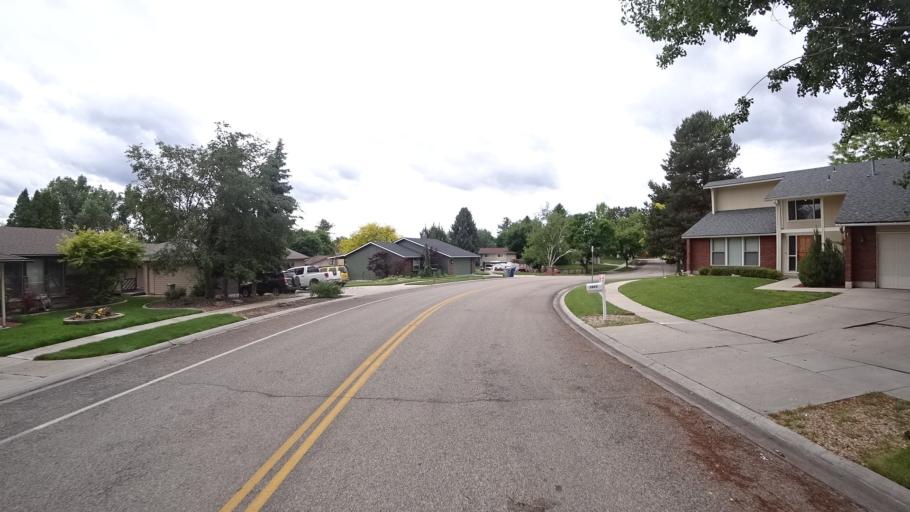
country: US
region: Idaho
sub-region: Ada County
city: Eagle
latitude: 43.7045
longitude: -116.3420
